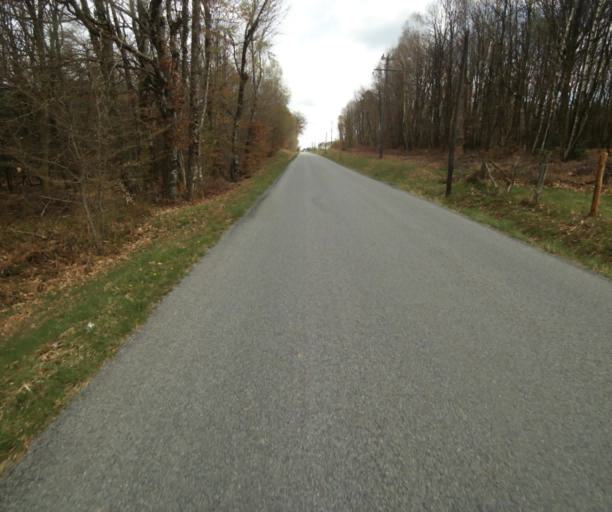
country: FR
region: Limousin
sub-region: Departement de la Correze
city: Laguenne
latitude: 45.2054
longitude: 1.8870
